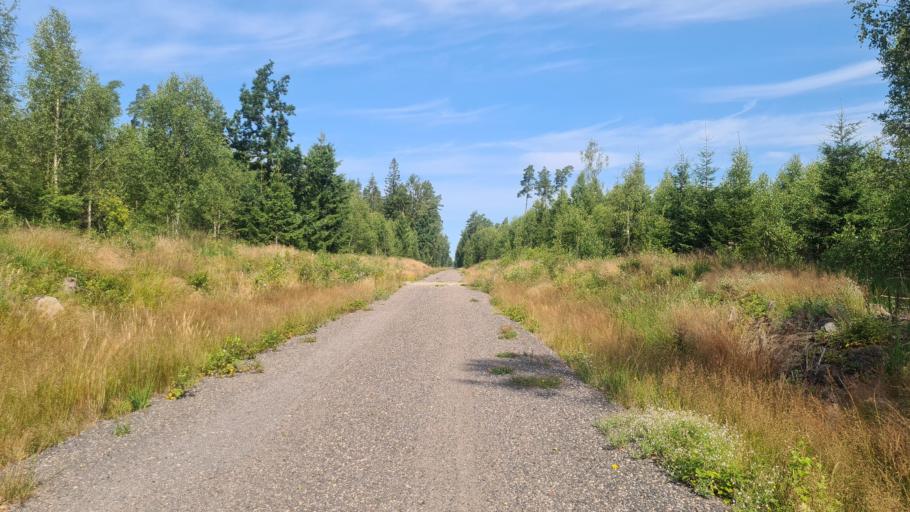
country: SE
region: Kronoberg
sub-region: Ljungby Kommun
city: Lagan
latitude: 56.9608
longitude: 13.9553
